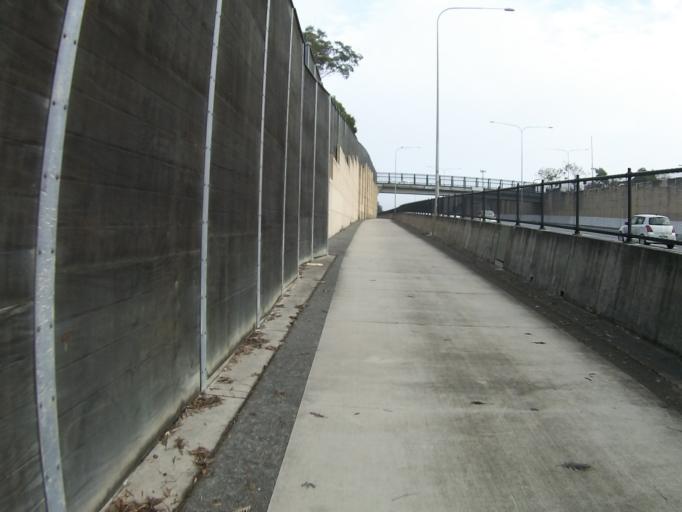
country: AU
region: Queensland
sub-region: Brisbane
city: Upper Mount Gravatt
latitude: -27.5652
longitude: 153.0819
